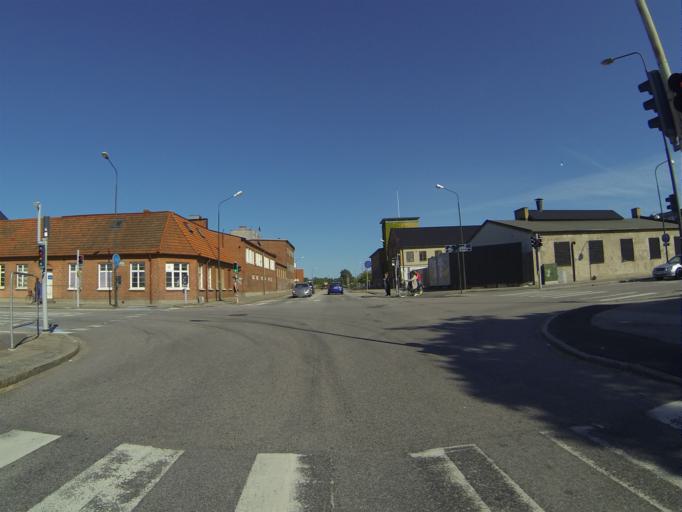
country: SE
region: Skane
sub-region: Malmo
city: Malmoe
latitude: 55.5984
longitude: 13.0298
